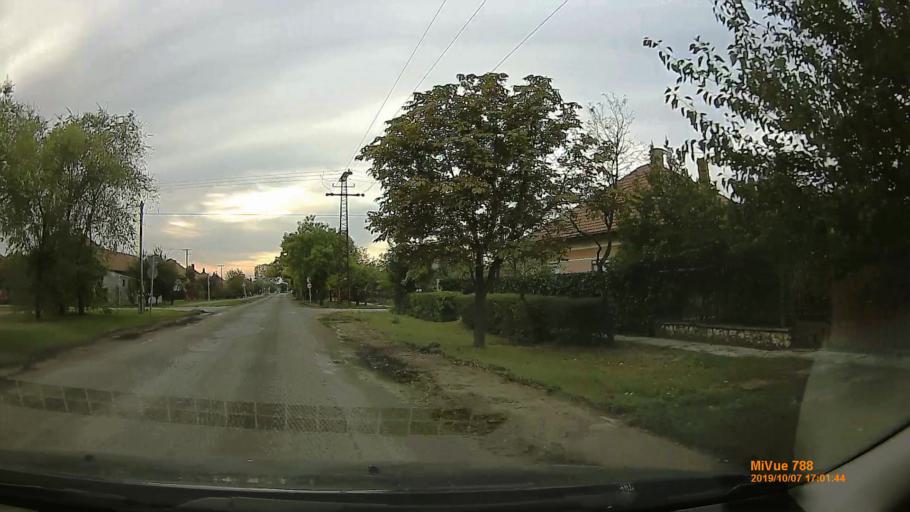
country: HU
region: Bekes
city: Szarvas
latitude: 46.8512
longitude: 20.5616
